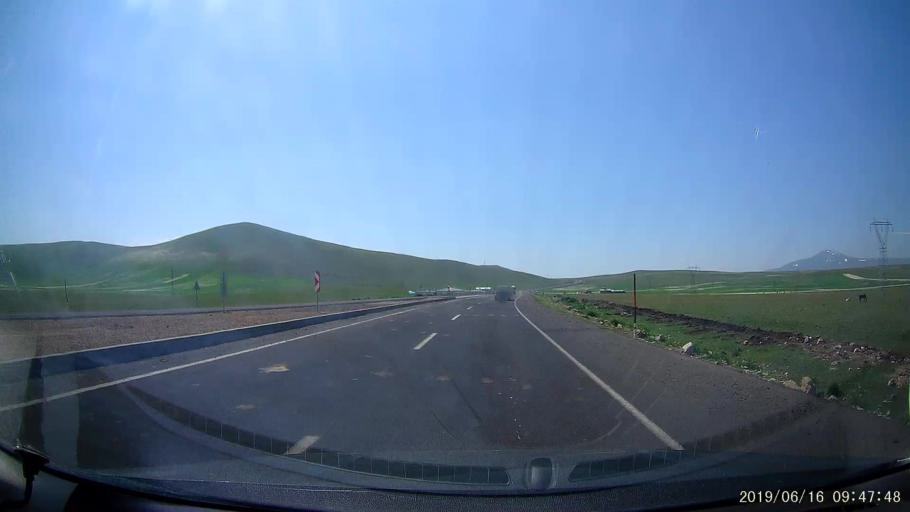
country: TR
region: Kars
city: Digor
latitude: 40.4410
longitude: 43.3481
